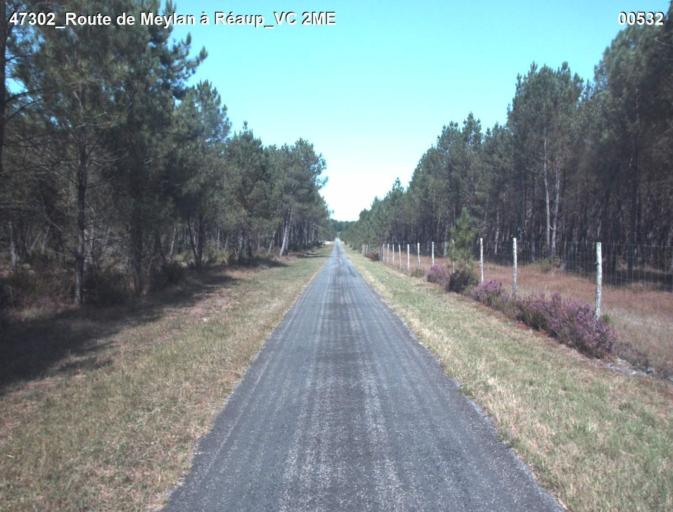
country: FR
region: Aquitaine
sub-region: Departement du Lot-et-Garonne
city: Mezin
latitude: 44.1035
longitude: 0.1378
